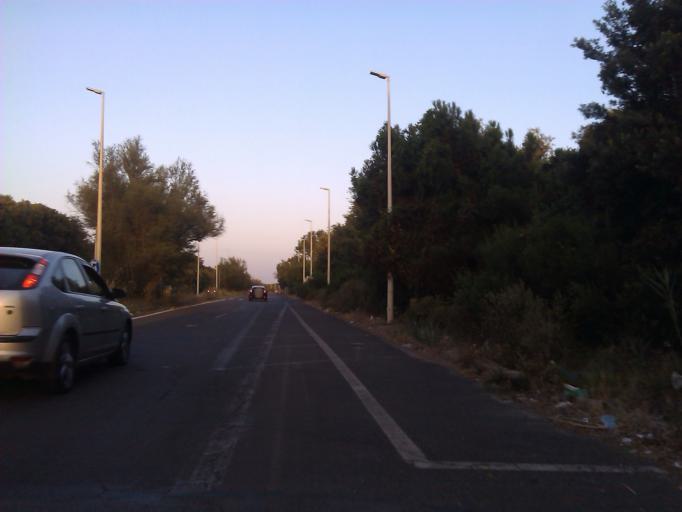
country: IT
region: Latium
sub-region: Citta metropolitana di Roma Capitale
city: Acilia-Castel Fusano-Ostia Antica
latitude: 41.7074
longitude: 12.3374
